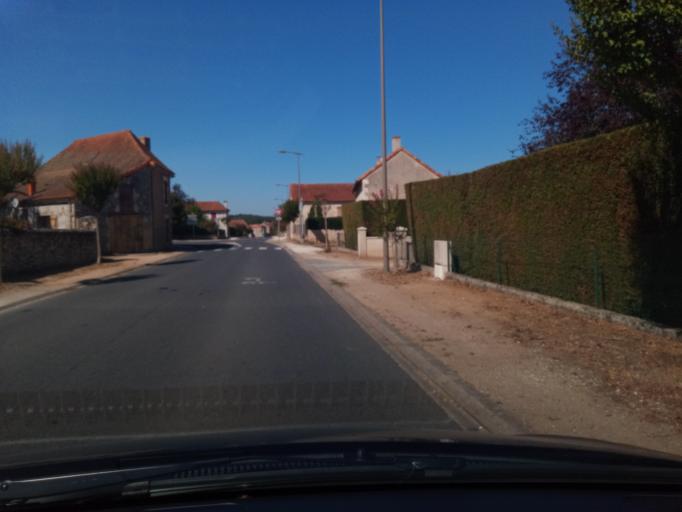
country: FR
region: Poitou-Charentes
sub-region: Departement de la Vienne
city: Montmorillon
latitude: 46.4901
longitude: 0.8425
